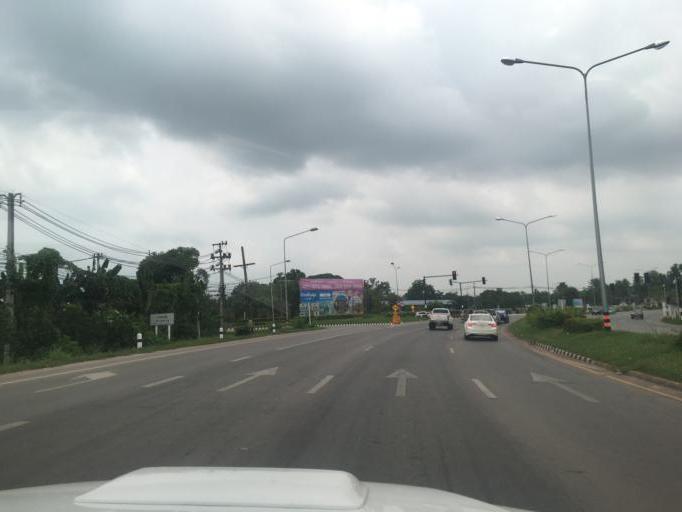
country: TH
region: Changwat Udon Thani
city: Udon Thani
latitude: 17.3892
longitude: 102.7660
